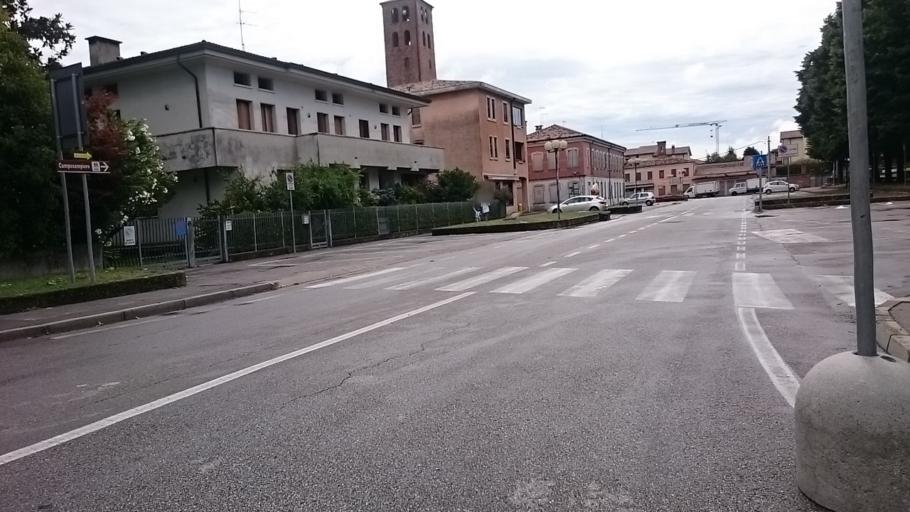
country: IT
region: Veneto
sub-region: Provincia di Padova
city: Camposampiero
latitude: 45.5730
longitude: 11.9314
